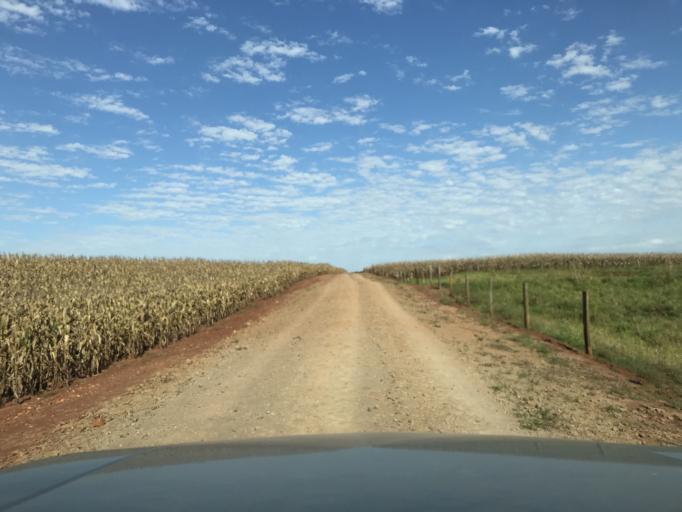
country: BR
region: Parana
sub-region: Palotina
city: Palotina
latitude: -24.1680
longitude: -53.7548
